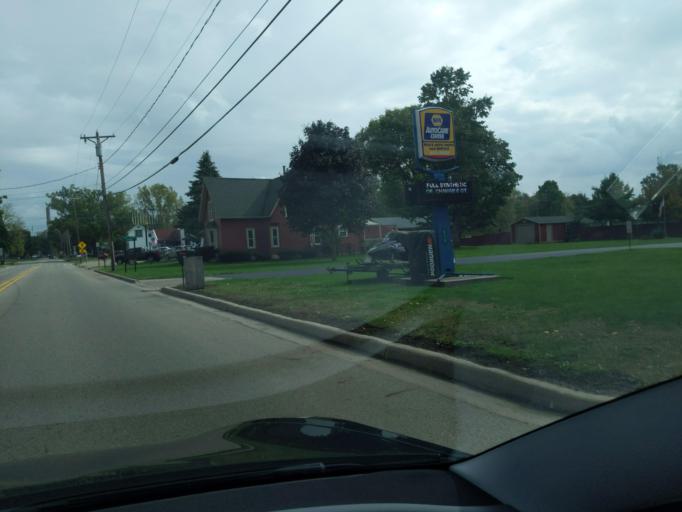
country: US
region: Michigan
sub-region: Eaton County
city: Eaton Rapids
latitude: 42.5162
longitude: -84.6616
